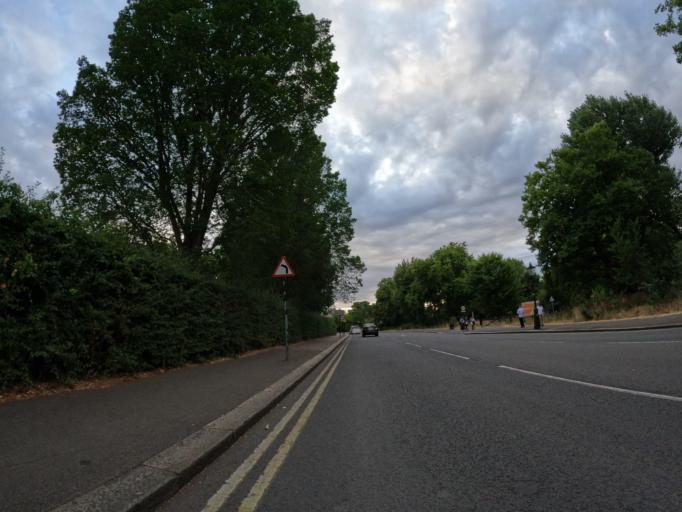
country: GB
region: England
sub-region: Greater London
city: Camden Town
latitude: 51.5364
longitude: -0.1504
